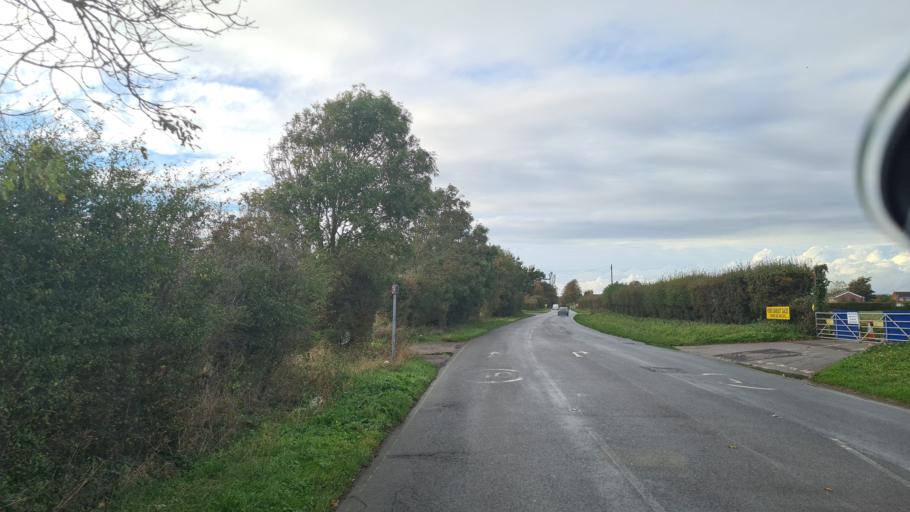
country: GB
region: England
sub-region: West Sussex
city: Walberton
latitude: 50.8133
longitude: -0.5954
